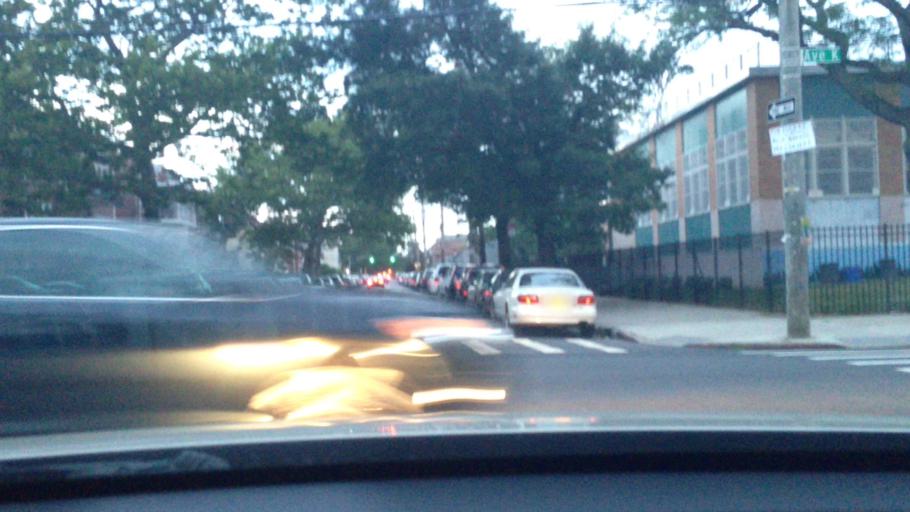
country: US
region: New York
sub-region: Kings County
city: East New York
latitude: 40.6332
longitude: -73.9081
